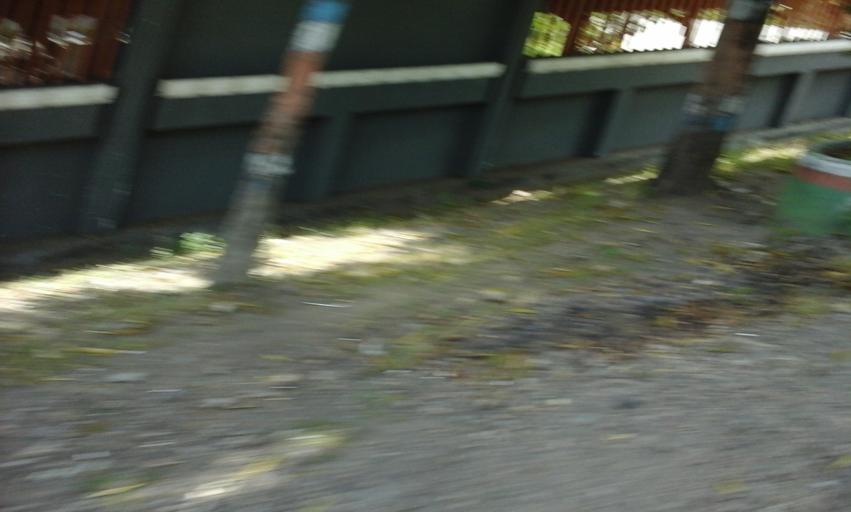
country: ID
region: East Java
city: Klatakan
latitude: -8.1573
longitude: 114.3937
